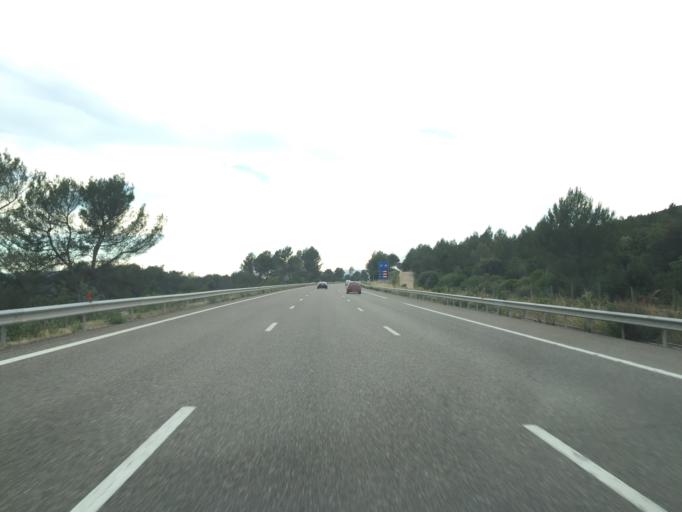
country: FR
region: Provence-Alpes-Cote d'Azur
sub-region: Departement du Var
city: La Celle
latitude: 43.4186
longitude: 6.0267
